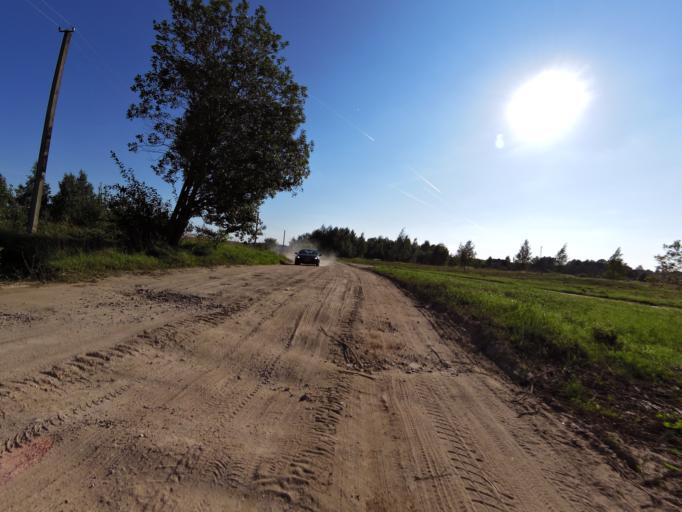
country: LT
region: Vilnius County
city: Pilaite
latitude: 54.7119
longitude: 25.1736
